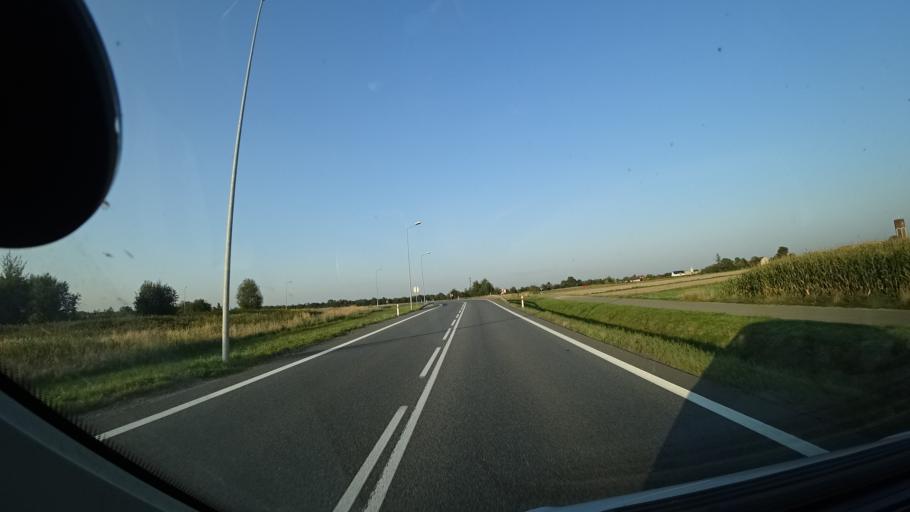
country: PL
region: Silesian Voivodeship
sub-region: Powiat gliwicki
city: Sosnicowice
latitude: 50.2808
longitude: 18.5766
